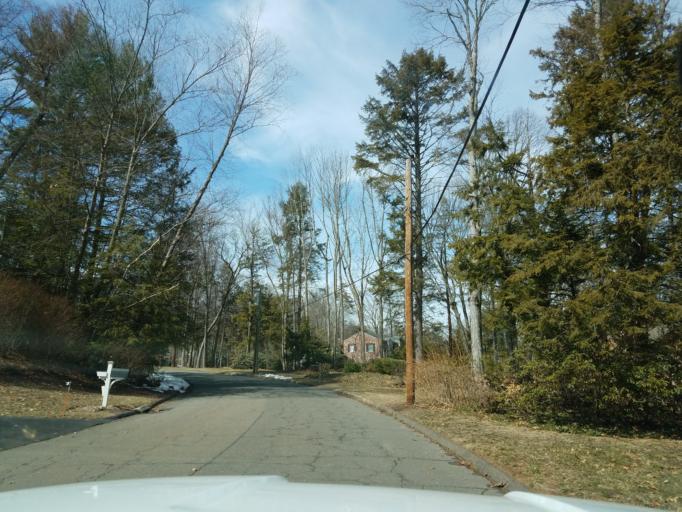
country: US
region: Connecticut
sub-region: Hartford County
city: Canton Valley
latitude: 41.7961
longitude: -72.8705
